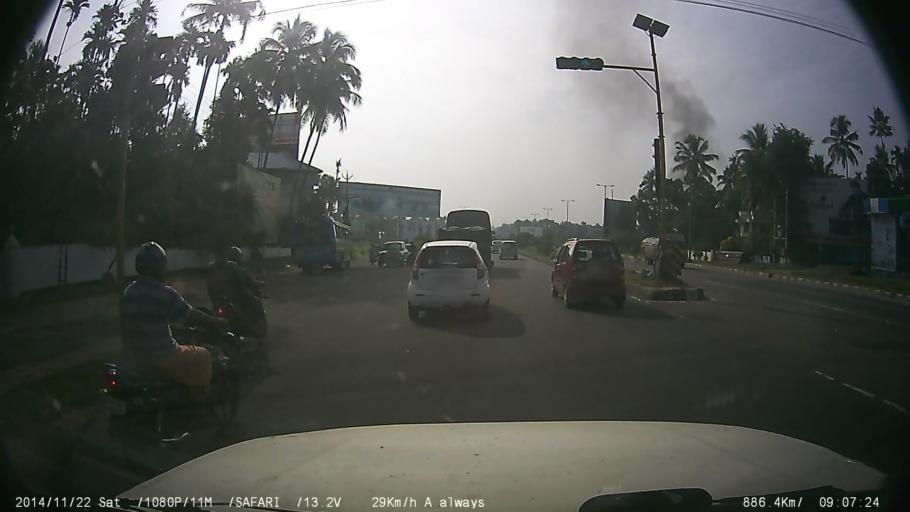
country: IN
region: Kerala
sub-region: Thrissur District
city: Kizhake Chalakudi
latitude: 10.3193
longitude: 76.3267
